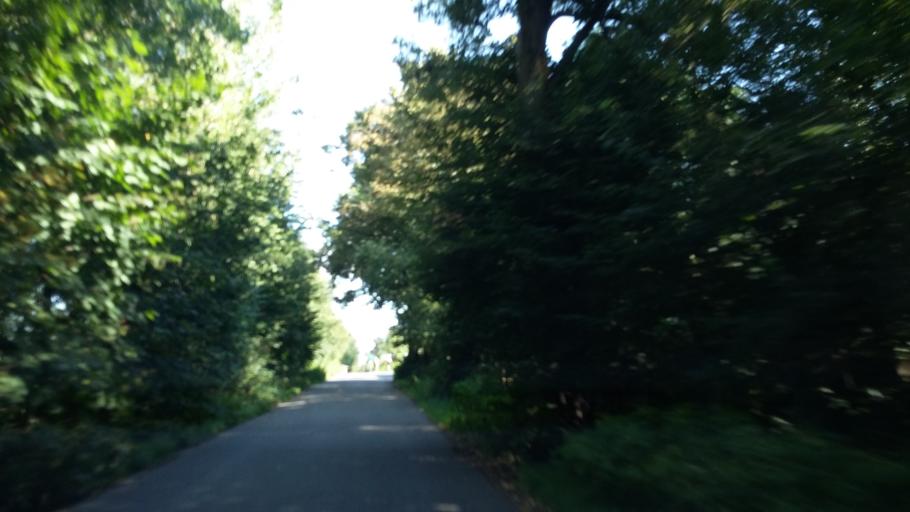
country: CZ
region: Liberecky
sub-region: Okres Semily
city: Turnov
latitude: 50.5984
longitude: 15.1781
